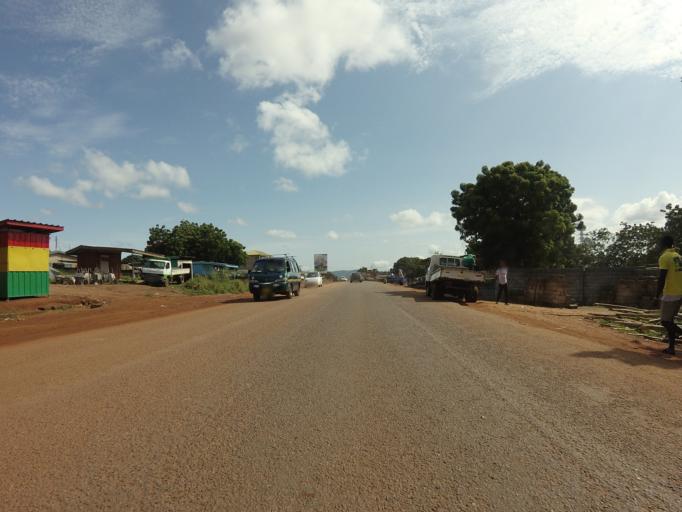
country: GH
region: Eastern
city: Aburi
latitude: 5.8138
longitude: -0.1221
